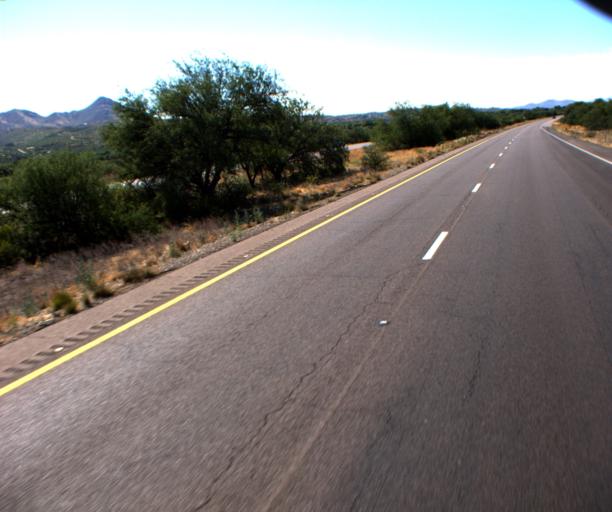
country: US
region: Arizona
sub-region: Santa Cruz County
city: Rio Rico
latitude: 31.5242
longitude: -111.0212
